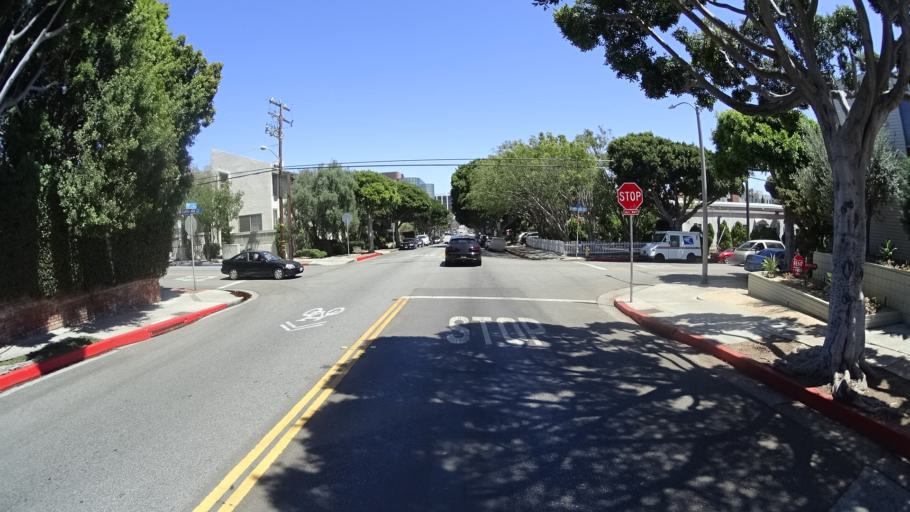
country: US
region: California
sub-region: Los Angeles County
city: Santa Monica
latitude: 34.0328
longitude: -118.4849
